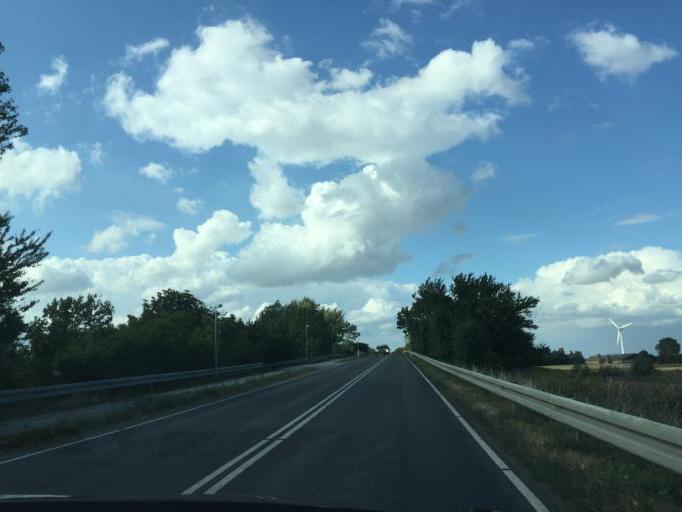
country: DK
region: South Denmark
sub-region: Faaborg-Midtfyn Kommune
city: Arslev
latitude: 55.3065
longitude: 10.4517
